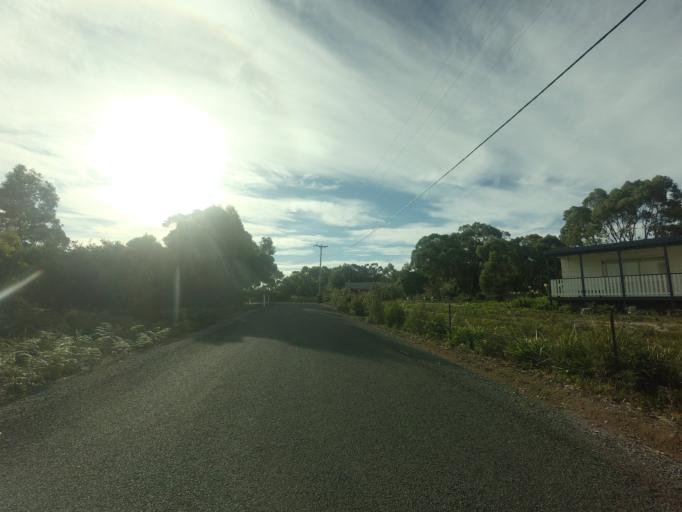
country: AU
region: Tasmania
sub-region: Sorell
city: Sorell
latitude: -42.9710
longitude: 147.8345
